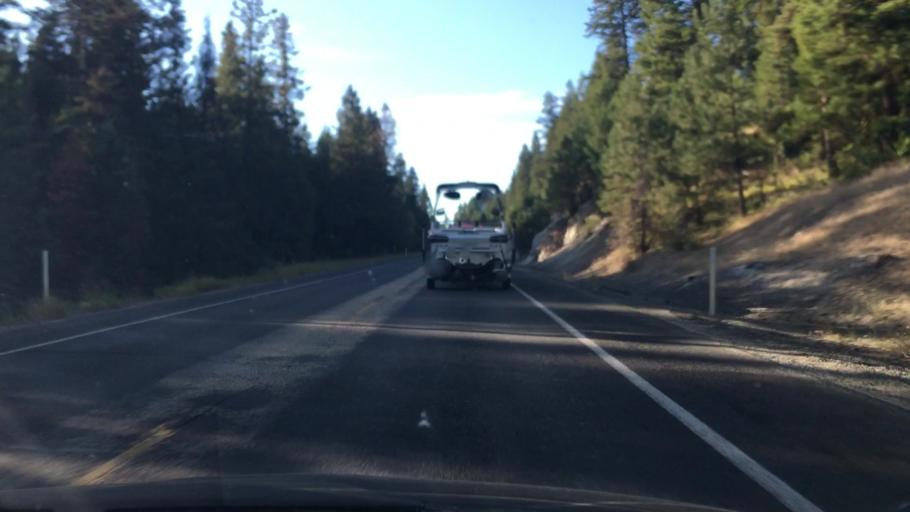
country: US
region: Idaho
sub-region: Valley County
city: Cascade
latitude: 44.5733
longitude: -116.0321
